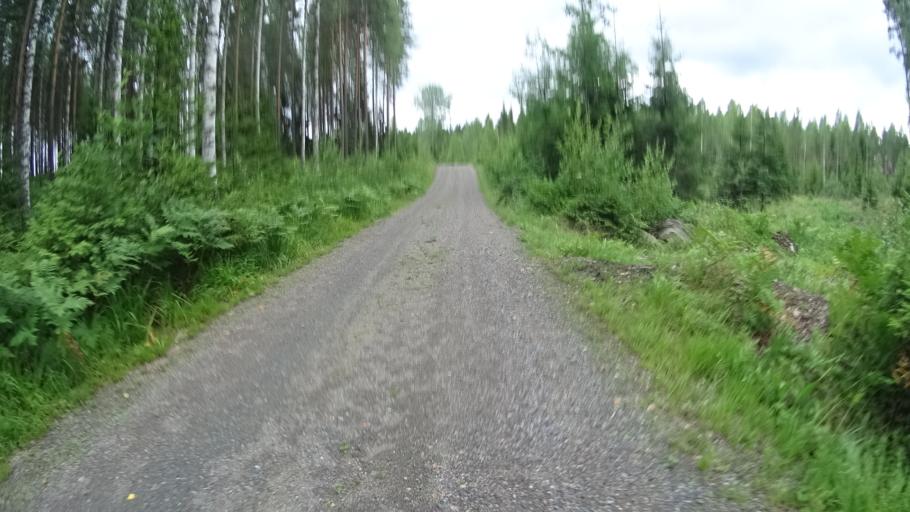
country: FI
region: Uusimaa
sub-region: Helsinki
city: Karkkila
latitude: 60.5640
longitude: 24.3292
